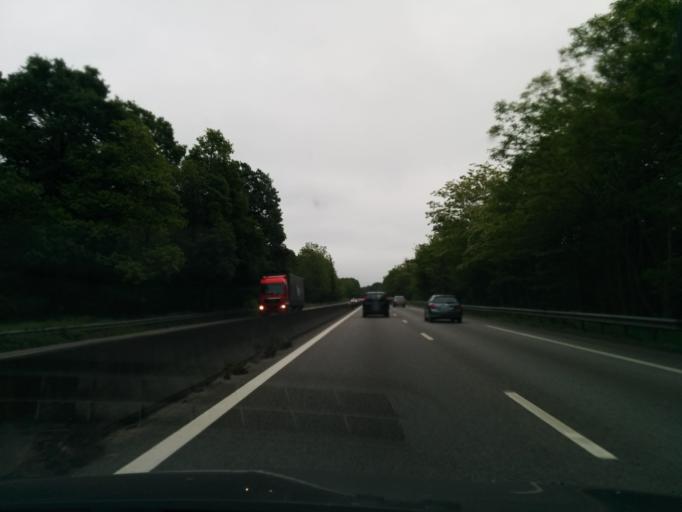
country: FR
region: Ile-de-France
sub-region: Departement des Yvelines
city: Noisy-le-Roi
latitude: 48.8542
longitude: 2.0605
